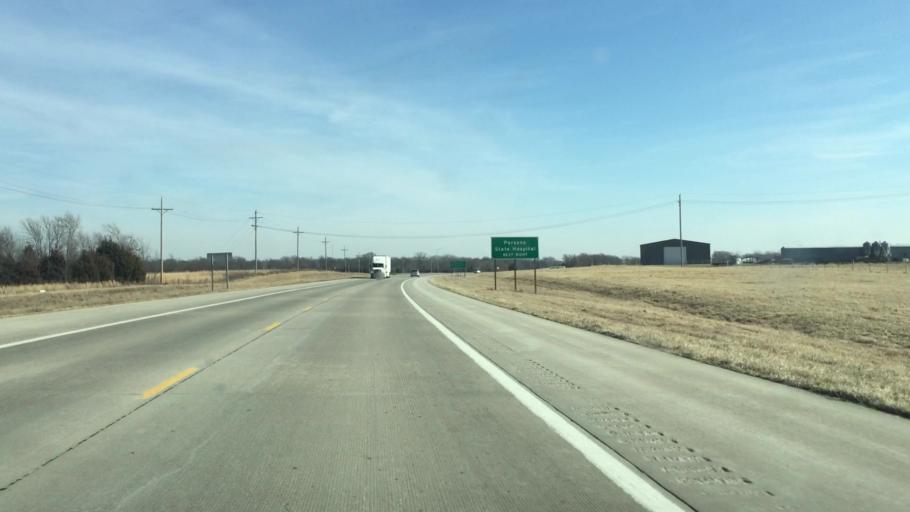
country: US
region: Kansas
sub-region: Labette County
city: Parsons
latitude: 37.3689
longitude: -95.2907
